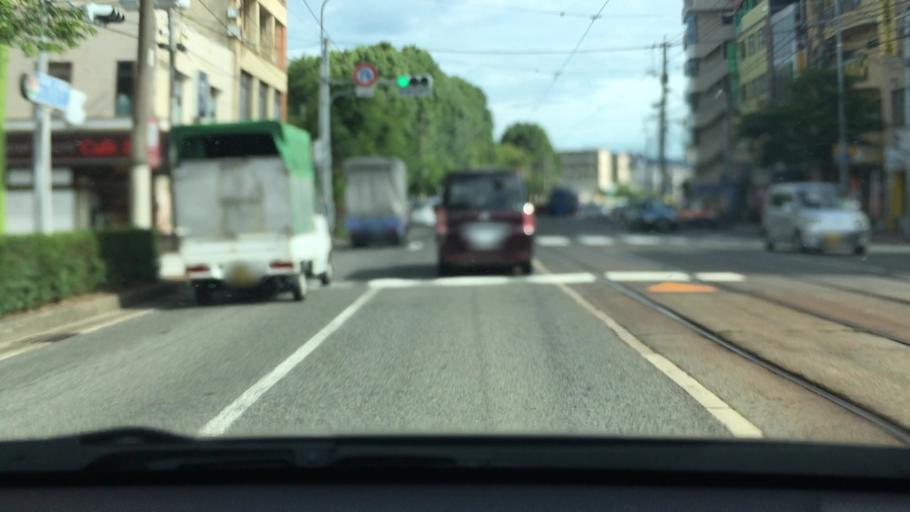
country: JP
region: Nagasaki
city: Obita
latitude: 32.7861
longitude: 129.8622
